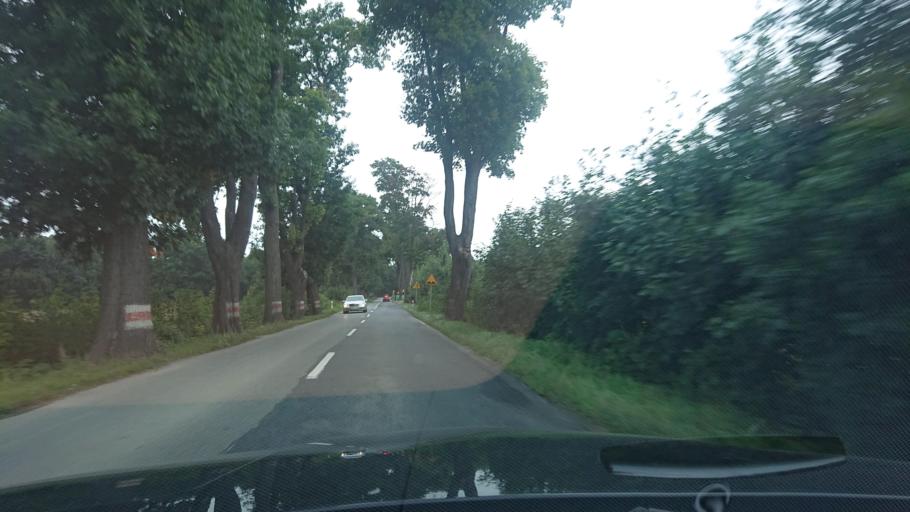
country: PL
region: Lower Silesian Voivodeship
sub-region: Powiat zabkowicki
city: Kamieniec Zabkowicki
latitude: 50.5092
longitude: 16.8700
